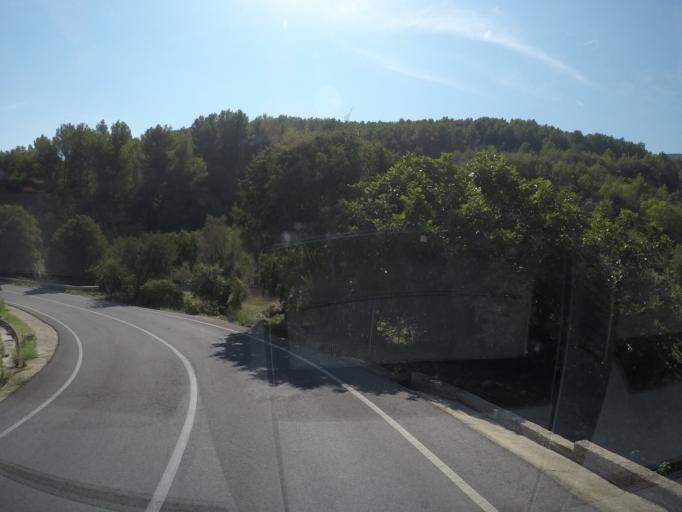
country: ES
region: Valencia
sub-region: Provincia de Alicante
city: Murla
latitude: 38.7795
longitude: -0.0988
